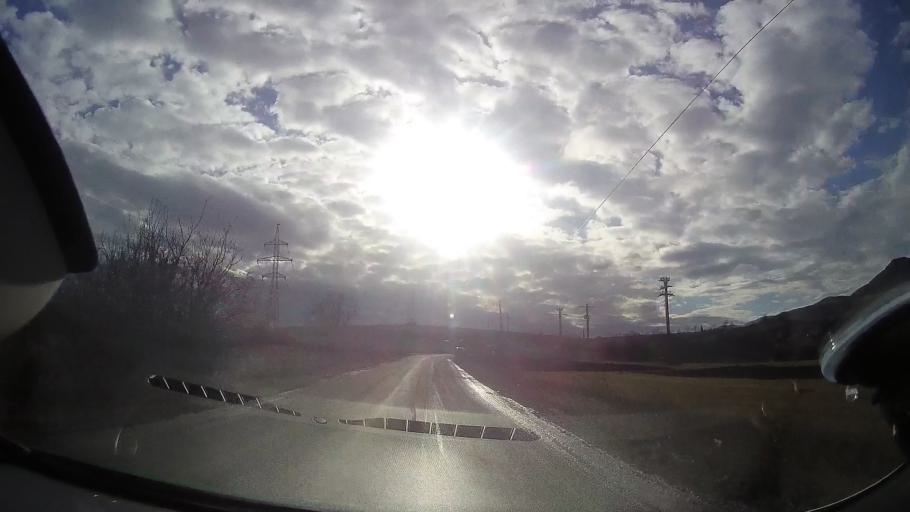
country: RO
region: Cluj
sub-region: Comuna Baisoara
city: Baisoara
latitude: 46.6238
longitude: 23.4524
